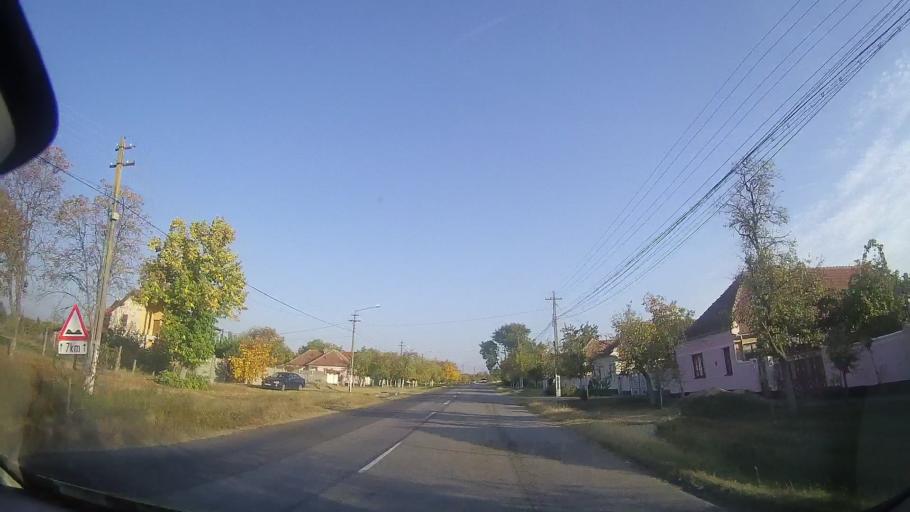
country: RO
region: Timis
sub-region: Comuna Fibis
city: Fibis
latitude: 45.9645
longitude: 21.4181
